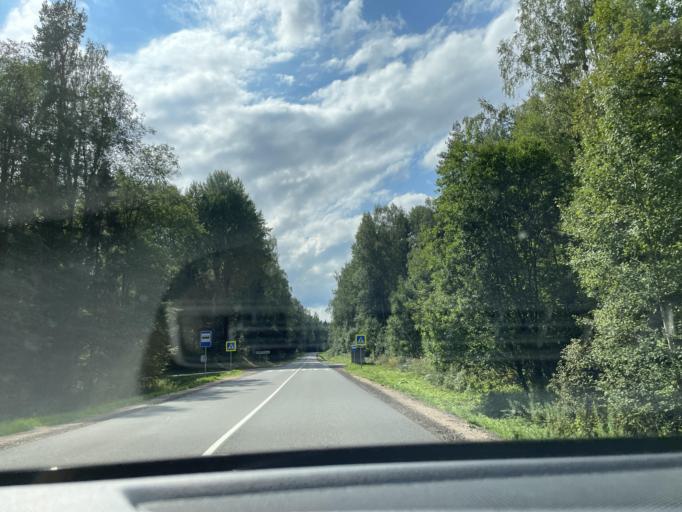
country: RU
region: Novgorod
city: Valday
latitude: 58.0334
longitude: 33.2166
